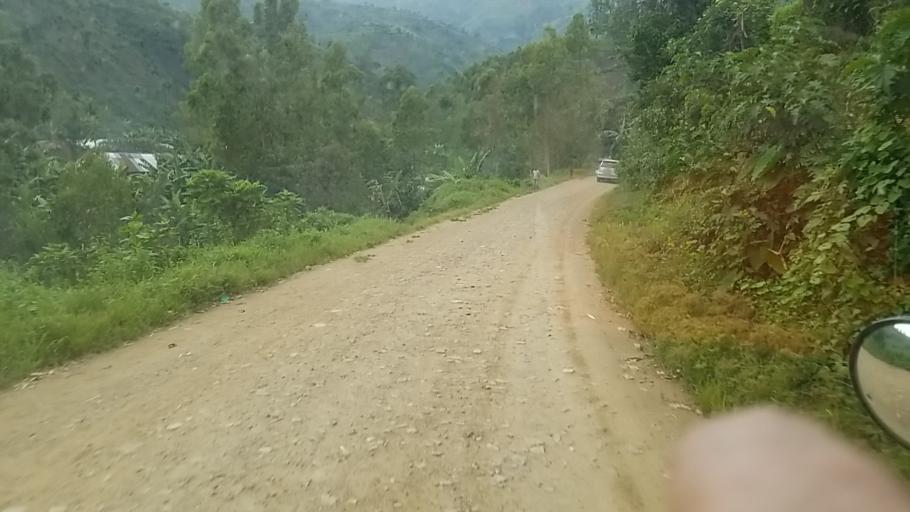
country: CD
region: Nord Kivu
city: Sake
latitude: -1.9529
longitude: 28.9266
